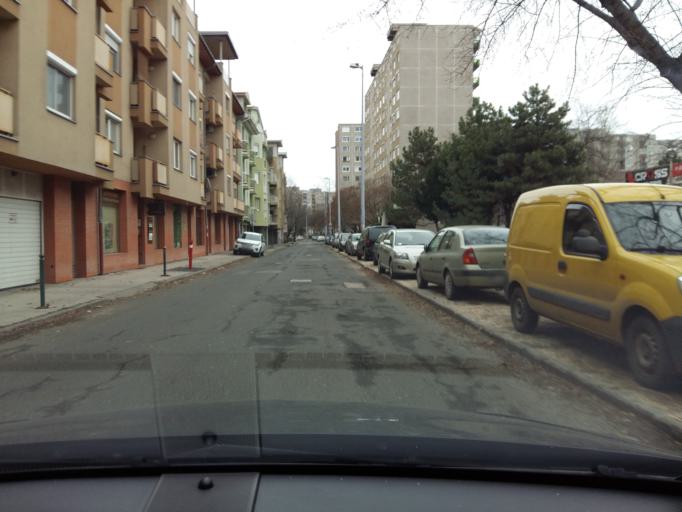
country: HU
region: Budapest
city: Budapest IV. keruelet
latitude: 47.5591
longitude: 19.0950
